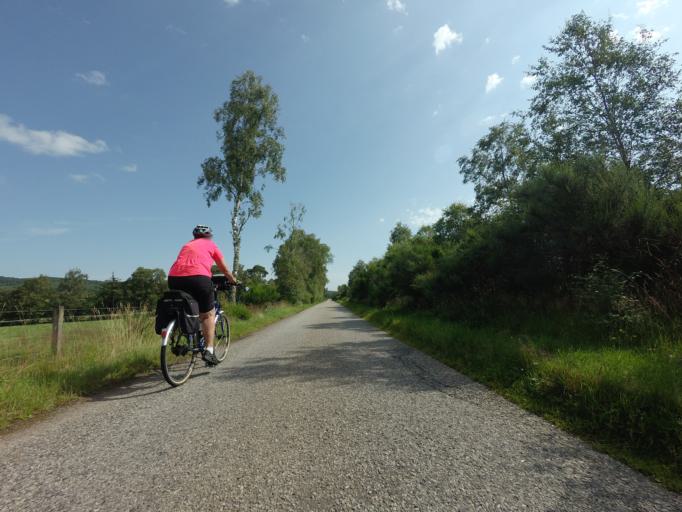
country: GB
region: Scotland
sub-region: Highland
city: Invergordon
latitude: 57.7463
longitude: -4.1702
